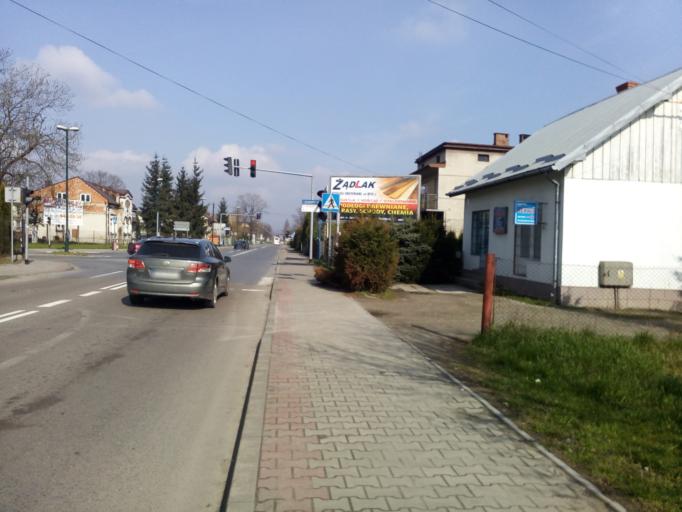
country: PL
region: Lesser Poland Voivodeship
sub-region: Powiat nowosadecki
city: Nowy Sacz
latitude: 49.6035
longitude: 20.7145
